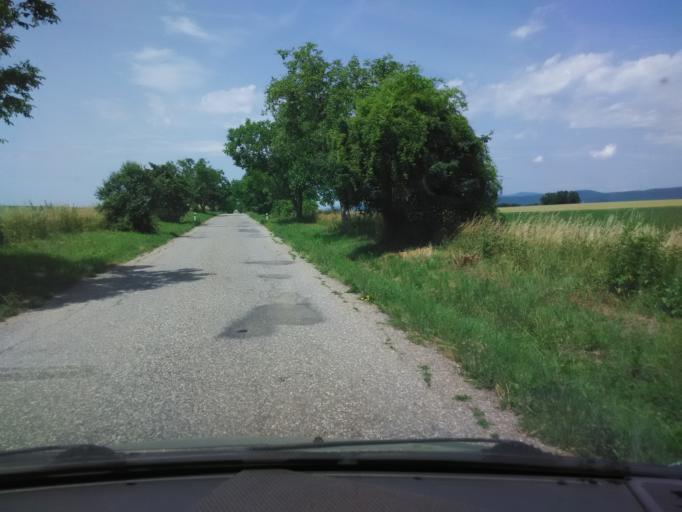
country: SK
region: Nitriansky
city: Levice
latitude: 48.2366
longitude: 18.6464
